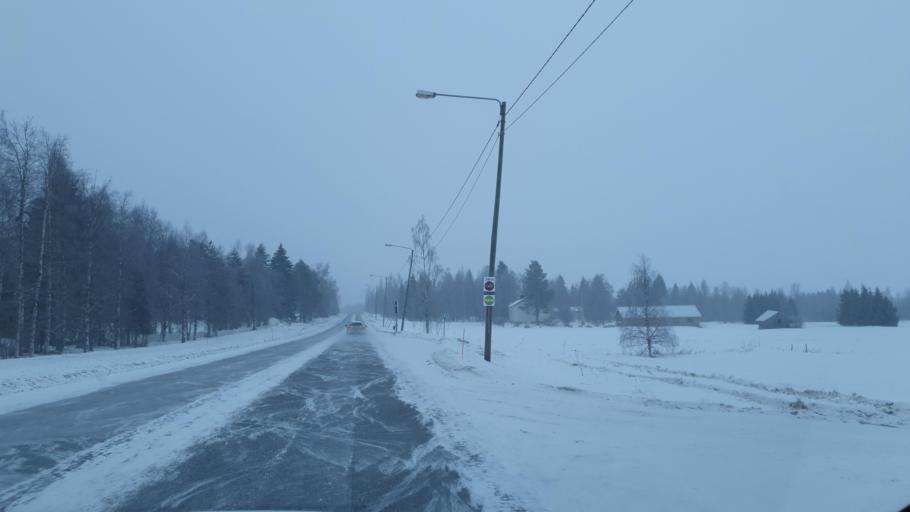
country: FI
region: Lapland
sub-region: Kemi-Tornio
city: Tornio
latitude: 66.0456
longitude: 24.0129
